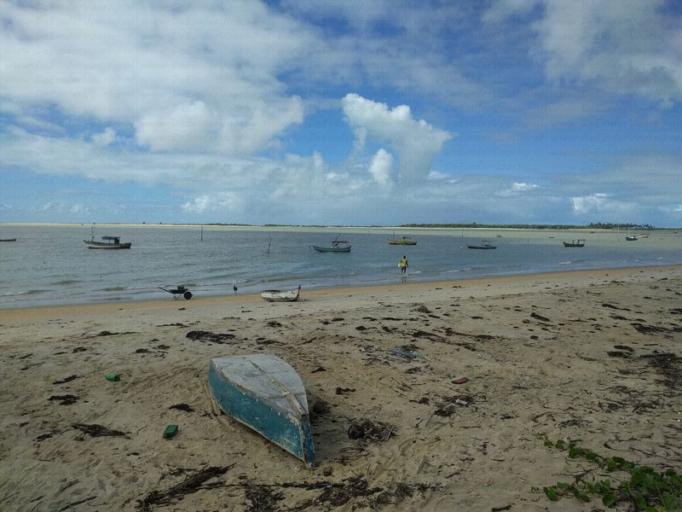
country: BR
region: Bahia
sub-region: Nova Vicosa
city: Nova Vicosa
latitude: -17.7335
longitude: -39.1850
